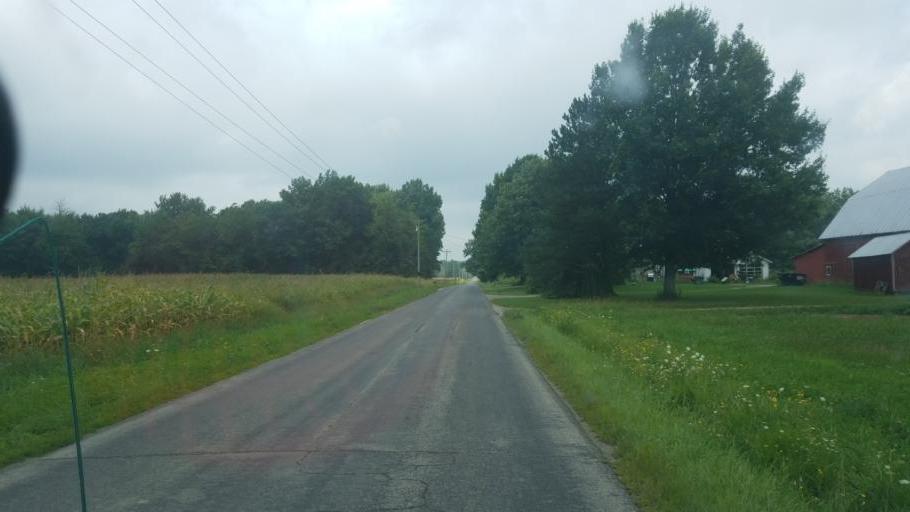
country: US
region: Ohio
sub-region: Huron County
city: Greenwich
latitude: 40.9810
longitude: -82.4734
